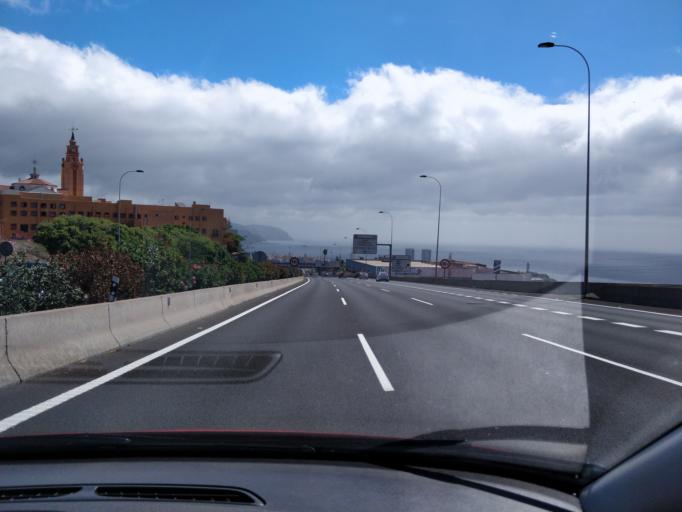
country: ES
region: Canary Islands
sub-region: Provincia de Santa Cruz de Tenerife
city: Santa Cruz de Tenerife
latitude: 28.4490
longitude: -16.2806
